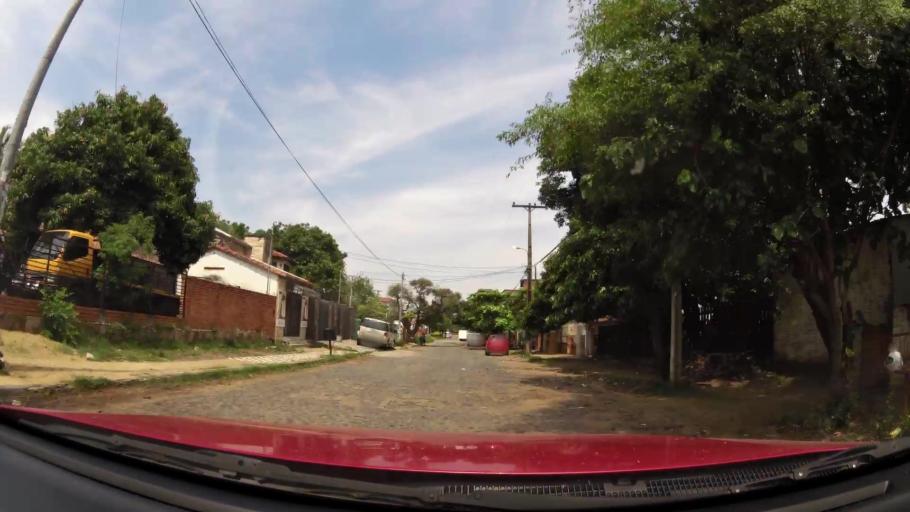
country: PY
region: Asuncion
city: Asuncion
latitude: -25.2684
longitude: -57.5862
